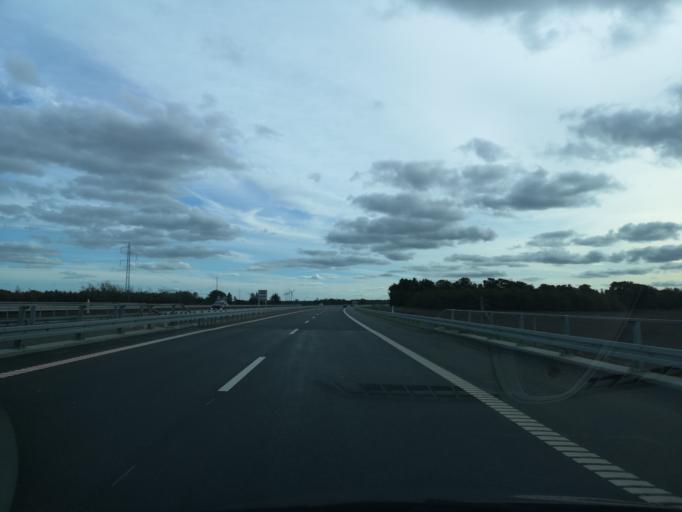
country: DK
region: Central Jutland
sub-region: Herning Kommune
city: Avlum
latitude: 56.3579
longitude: 8.7328
